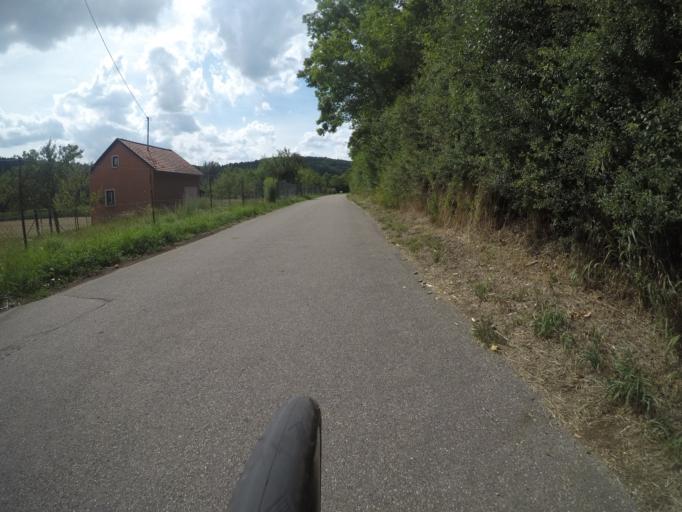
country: DE
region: Baden-Wuerttemberg
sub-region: Regierungsbezirk Stuttgart
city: Weil der Stadt
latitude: 48.7285
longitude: 8.8861
